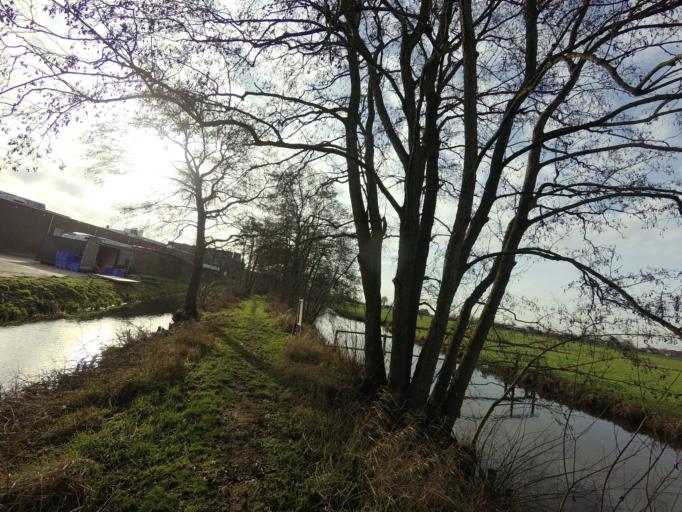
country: NL
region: Utrecht
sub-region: Gemeente Oudewater
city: Oudewater
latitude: 52.0377
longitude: 4.8644
